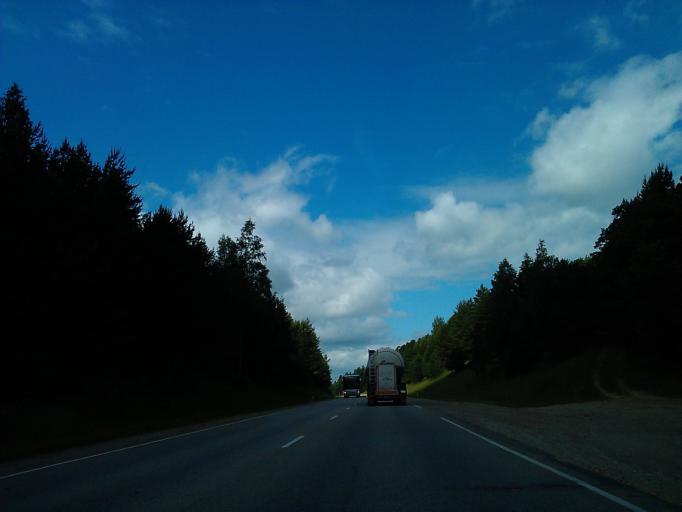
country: LV
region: Tukuma Rajons
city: Tukums
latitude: 56.9446
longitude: 23.1467
